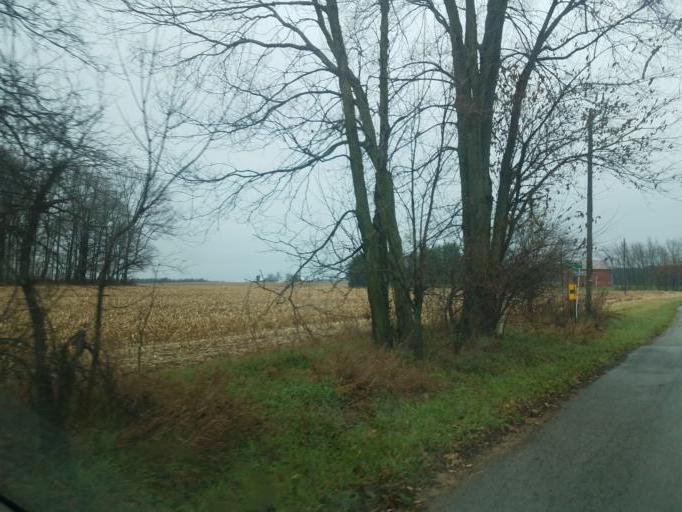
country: US
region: Ohio
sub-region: Knox County
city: Fredericktown
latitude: 40.5214
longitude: -82.5676
